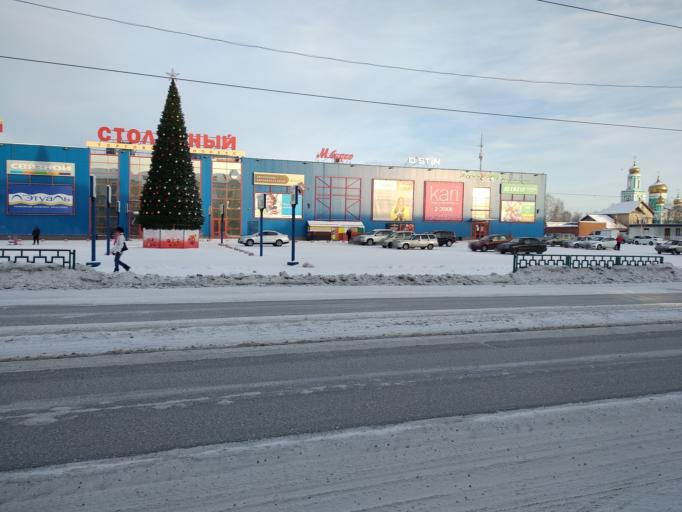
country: RU
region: Sverdlovsk
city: Krasnotur'insk
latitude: 59.7667
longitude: 60.2045
